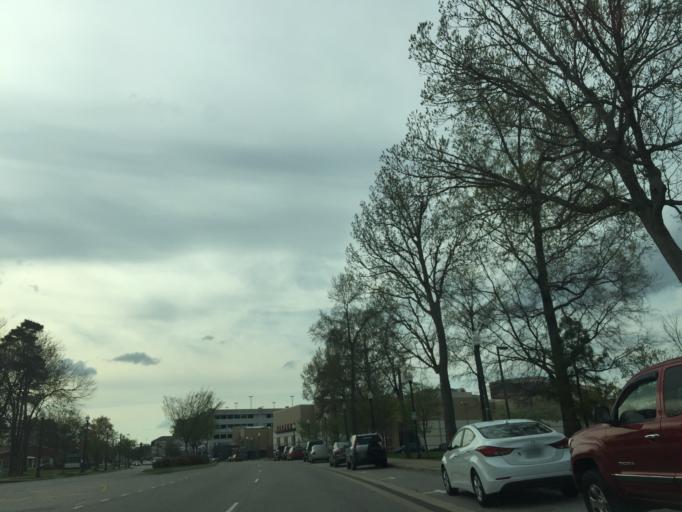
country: US
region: Virginia
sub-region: City of Newport News
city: Newport News
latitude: 37.0846
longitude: -76.4699
